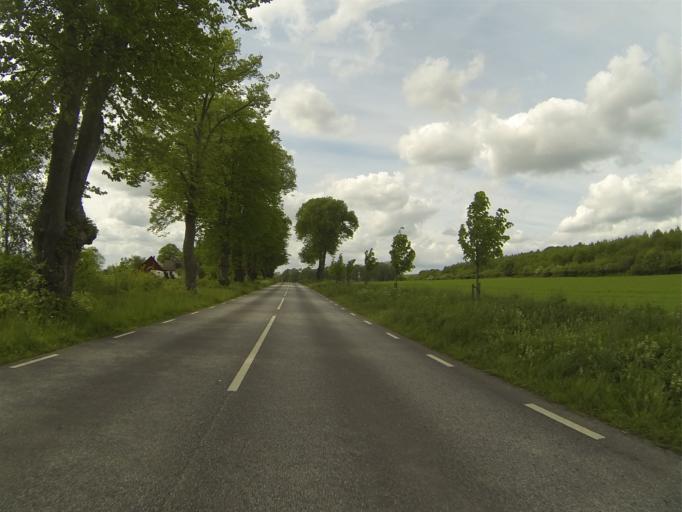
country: SE
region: Skane
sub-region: Sjobo Kommun
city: Sjoebo
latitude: 55.6731
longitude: 13.6619
